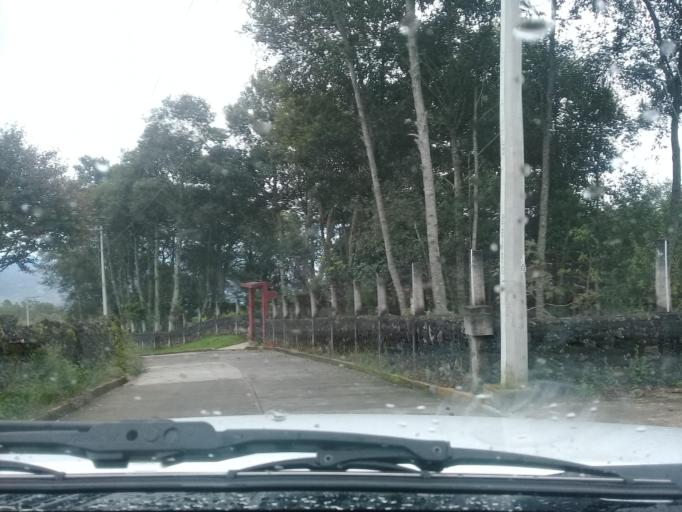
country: MX
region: Veracruz
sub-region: Acajete
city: La Joya
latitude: 19.6162
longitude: -97.0017
